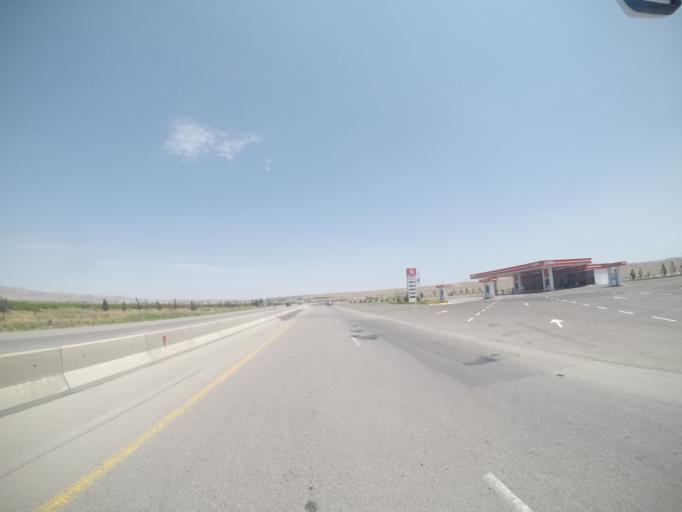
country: AZ
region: Haciqabul
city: Haciqabul
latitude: 40.0122
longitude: 48.9200
